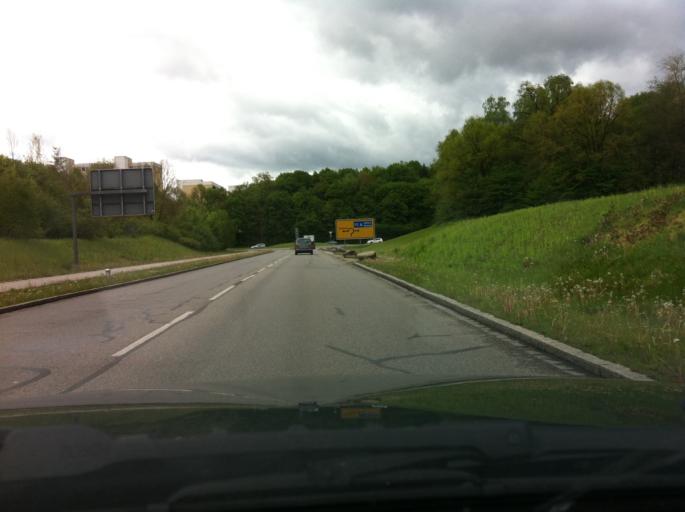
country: DE
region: Bavaria
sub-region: Upper Bavaria
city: Unterhaching
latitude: 48.0559
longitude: 11.5966
